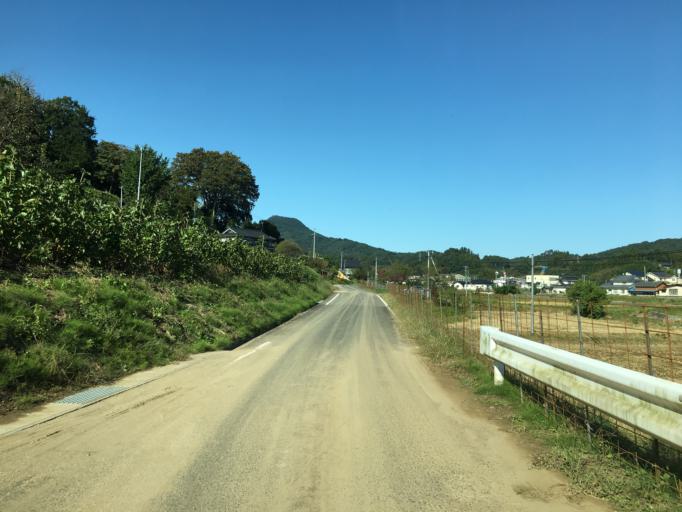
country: JP
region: Fukushima
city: Fukushima-shi
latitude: 37.6784
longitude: 140.5628
